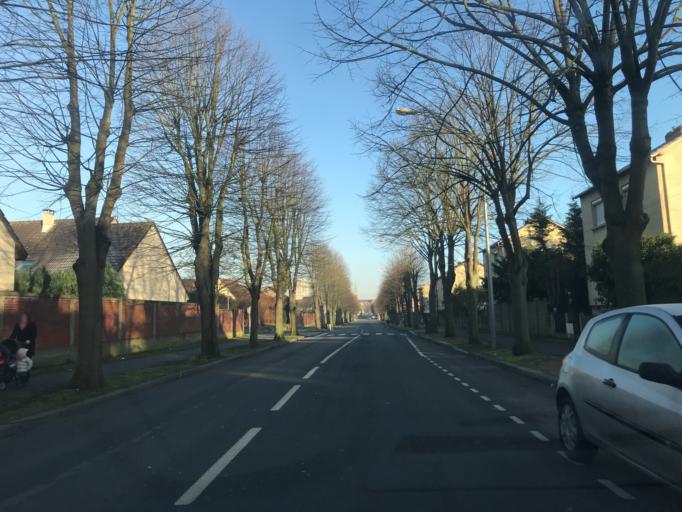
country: FR
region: Haute-Normandie
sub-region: Departement de la Seine-Maritime
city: Sotteville-les-Rouen
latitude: 49.4097
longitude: 1.1005
